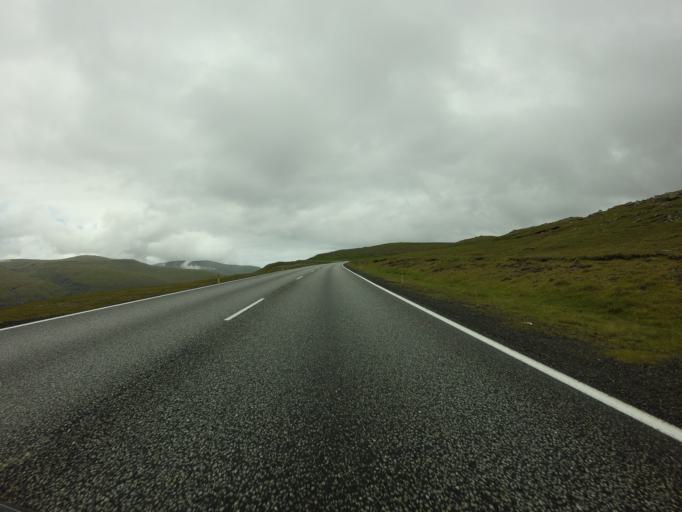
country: FO
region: Streymoy
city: Vestmanna
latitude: 62.1216
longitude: -7.1339
